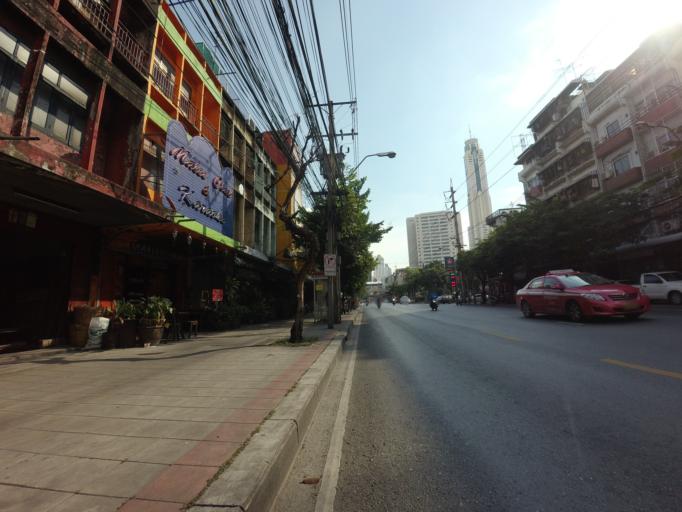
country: TH
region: Bangkok
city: Ratchathewi
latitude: 13.7593
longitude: 100.5425
